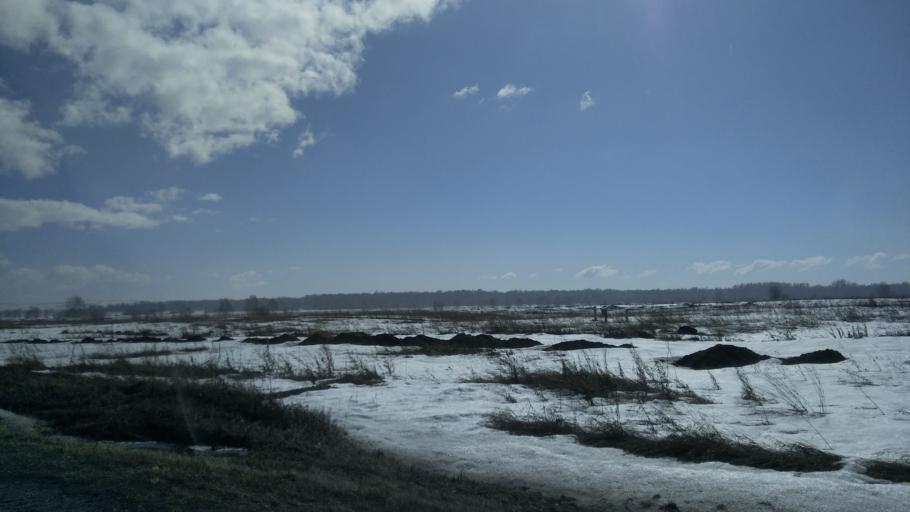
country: RU
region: Kemerovo
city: Yurga
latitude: 55.6834
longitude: 85.0072
